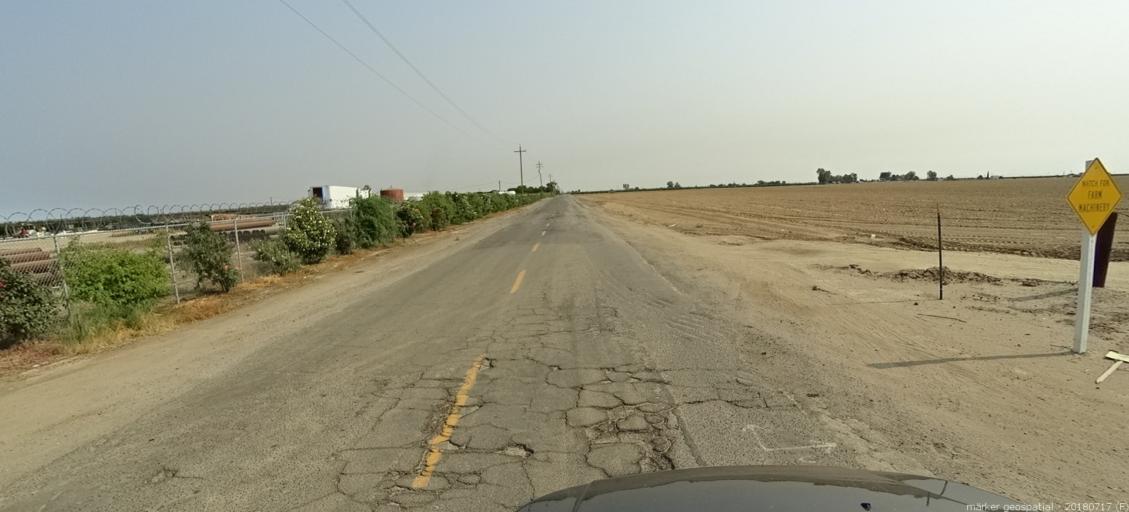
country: US
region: California
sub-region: Madera County
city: Madera Acres
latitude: 37.0835
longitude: -120.1109
